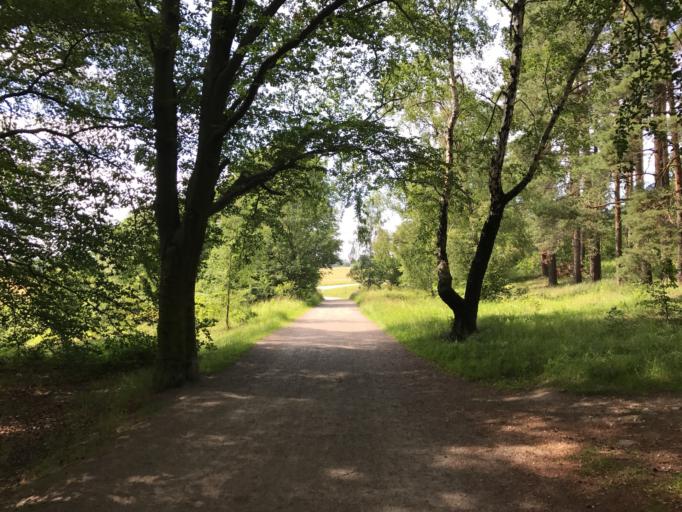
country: SE
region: Stockholm
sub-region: Lidingo
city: Lidingoe
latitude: 59.3341
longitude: 18.1240
